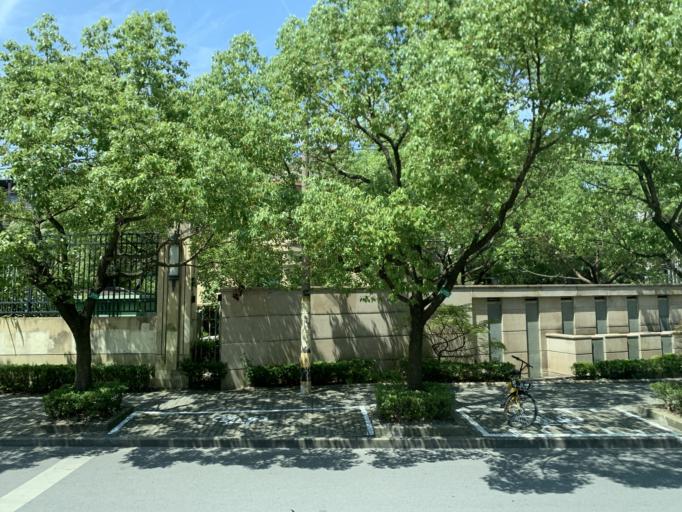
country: CN
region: Shanghai Shi
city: Huamu
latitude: 31.1786
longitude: 121.5340
